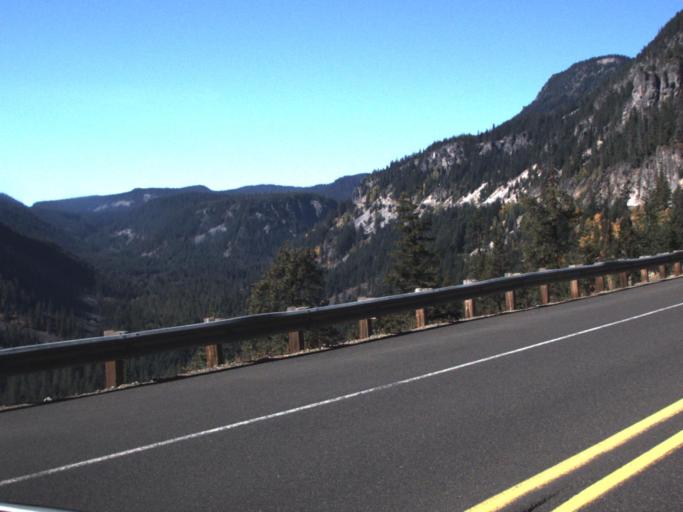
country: US
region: Washington
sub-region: Yakima County
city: Tieton
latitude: 46.6546
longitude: -121.3029
